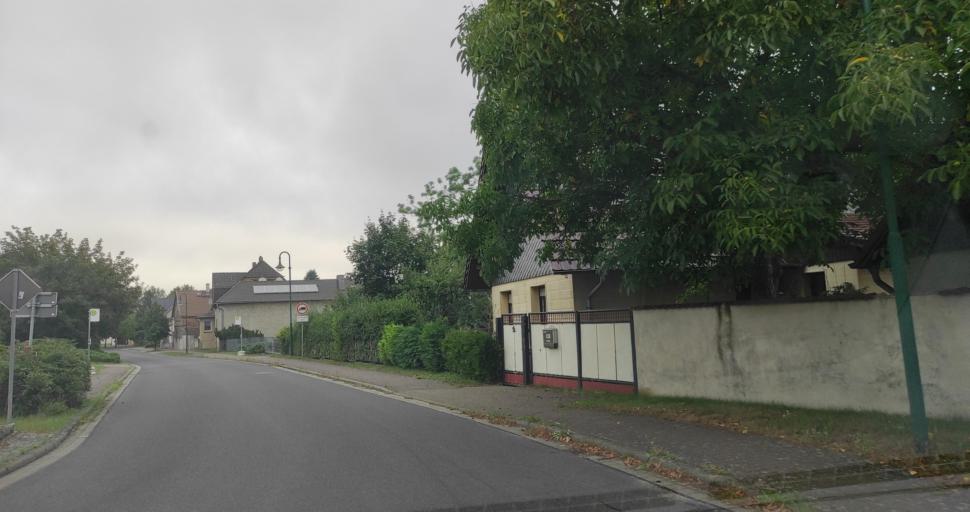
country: DE
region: Brandenburg
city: Heinersbruck
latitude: 51.7455
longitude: 14.5451
